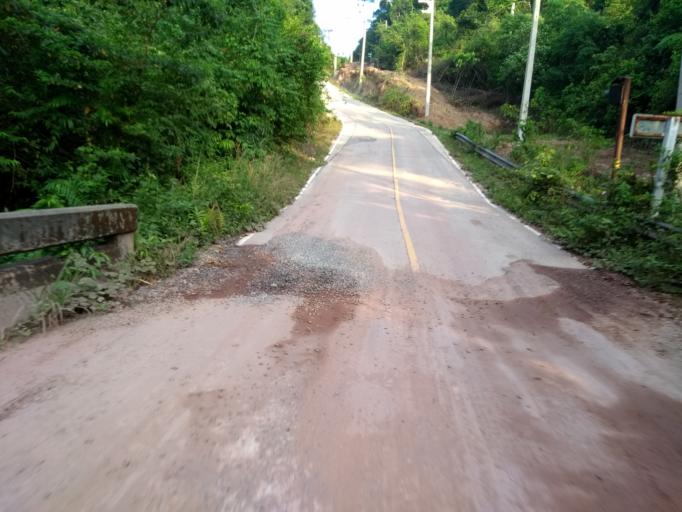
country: TH
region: Trat
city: Ko Kut
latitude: 11.6022
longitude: 102.5674
